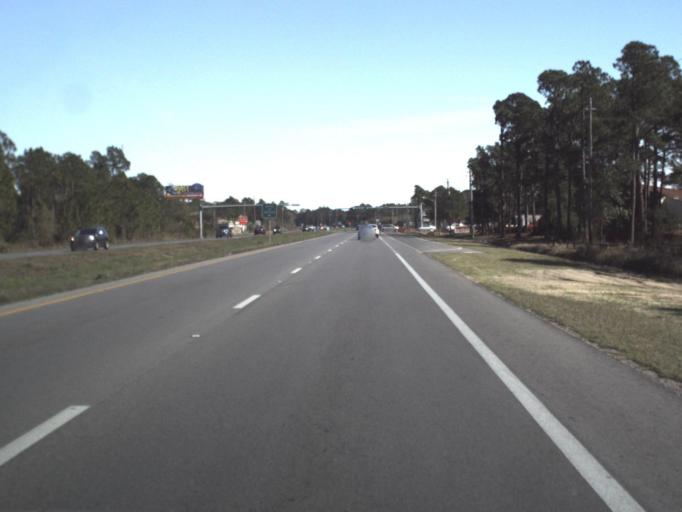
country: US
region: Florida
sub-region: Bay County
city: Panama City Beach
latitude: 30.1912
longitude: -85.7951
